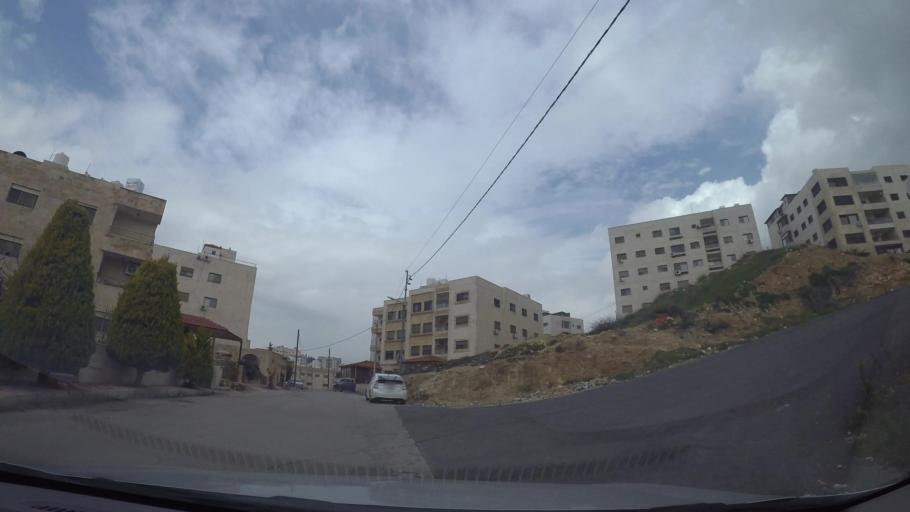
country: JO
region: Amman
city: Umm as Summaq
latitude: 31.9077
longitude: 35.8501
